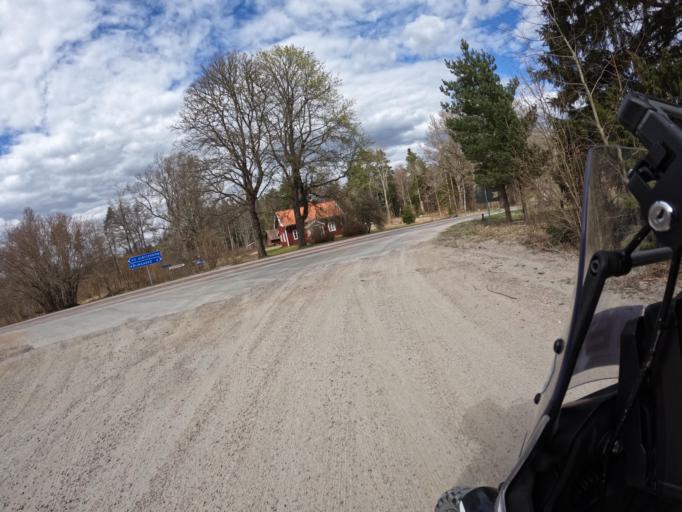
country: SE
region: Joenkoeping
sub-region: Mullsjo Kommun
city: Mullsjoe
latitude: 57.9032
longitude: 13.6536
